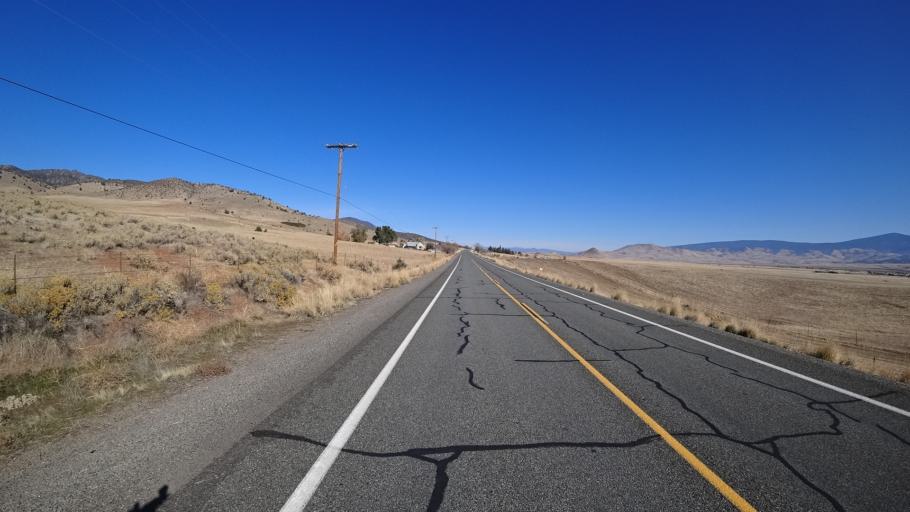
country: US
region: California
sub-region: Siskiyou County
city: Montague
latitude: 41.7823
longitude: -122.5197
